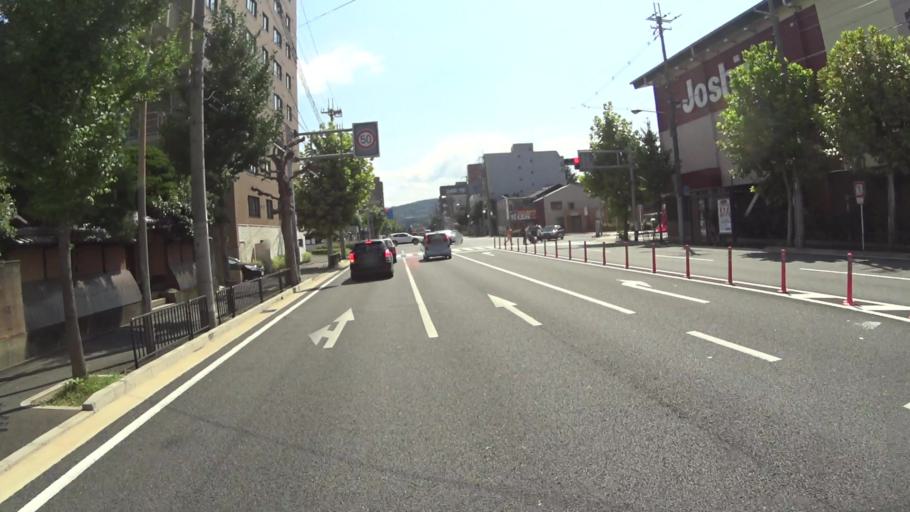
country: JP
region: Kyoto
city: Kyoto
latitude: 34.9822
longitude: 135.7639
